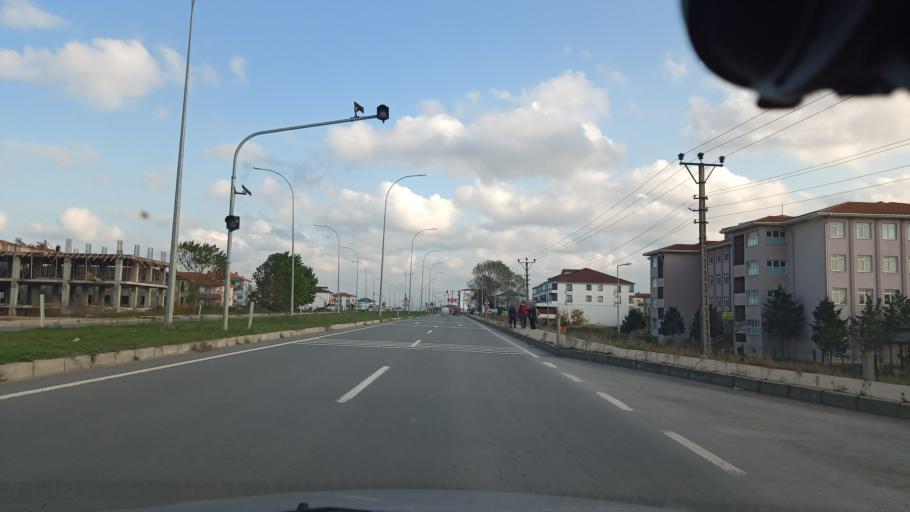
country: TR
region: Sakarya
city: Karasu
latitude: 41.1012
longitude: 30.7022
